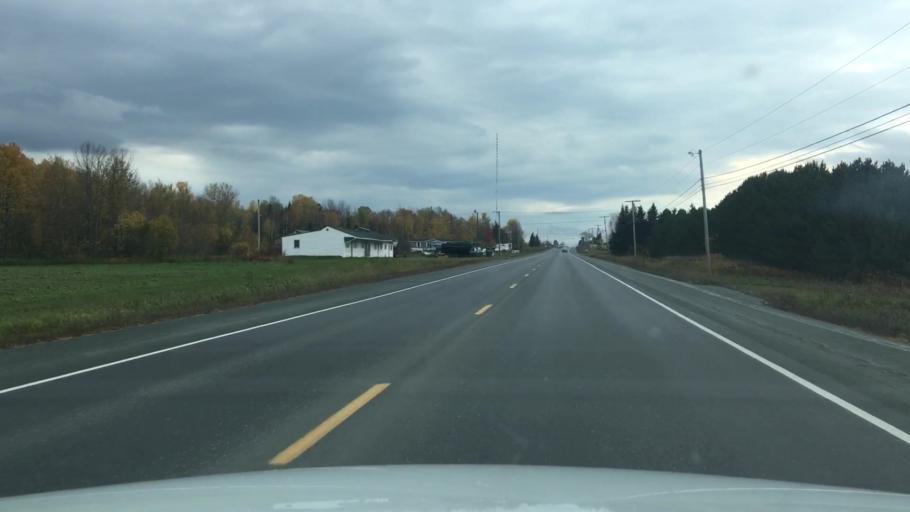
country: US
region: Maine
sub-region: Aroostook County
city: Caribou
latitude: 46.7728
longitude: -67.9895
